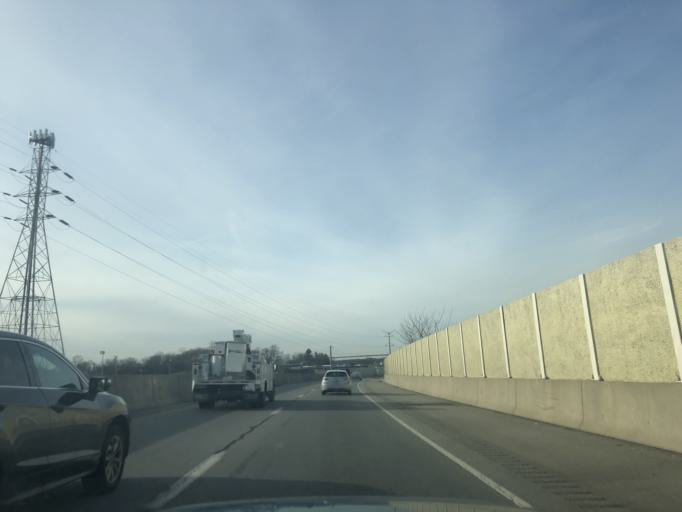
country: US
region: Pennsylvania
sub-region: Montgomery County
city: Wyndmoor
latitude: 40.1010
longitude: -75.1917
